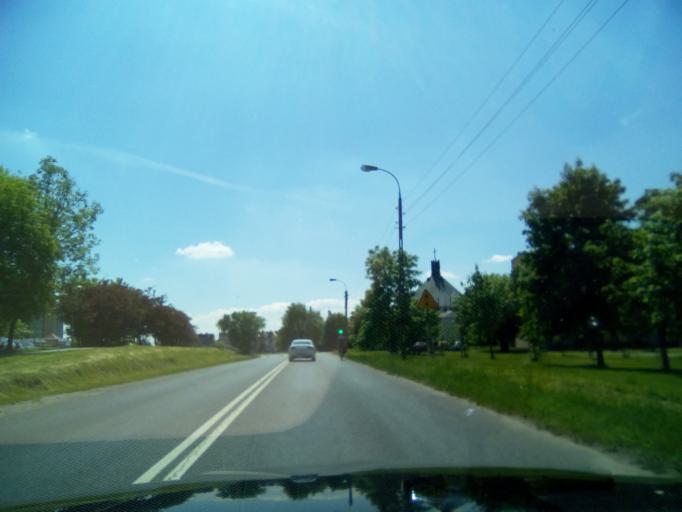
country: PL
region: Greater Poland Voivodeship
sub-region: Powiat gnieznienski
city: Gniezno
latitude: 52.5510
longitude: 17.6039
